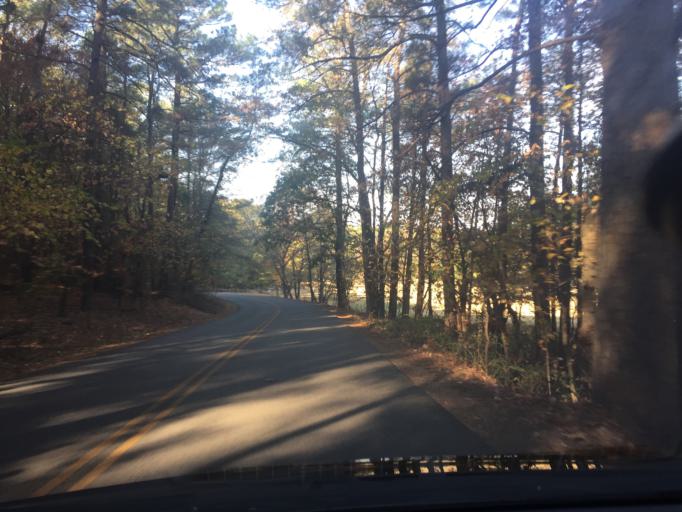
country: US
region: Georgia
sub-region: Cobb County
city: Marietta
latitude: 33.9828
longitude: -84.5756
